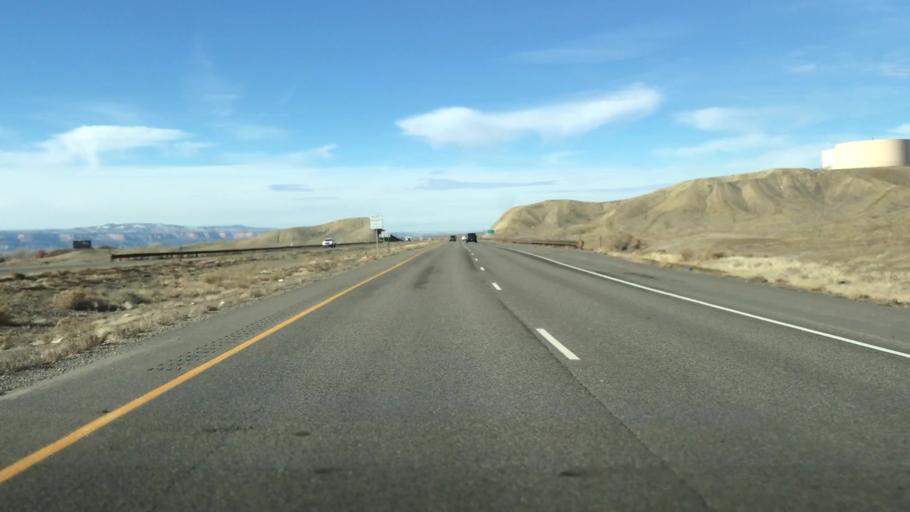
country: US
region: Colorado
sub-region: Mesa County
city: Clifton
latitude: 39.1031
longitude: -108.4556
